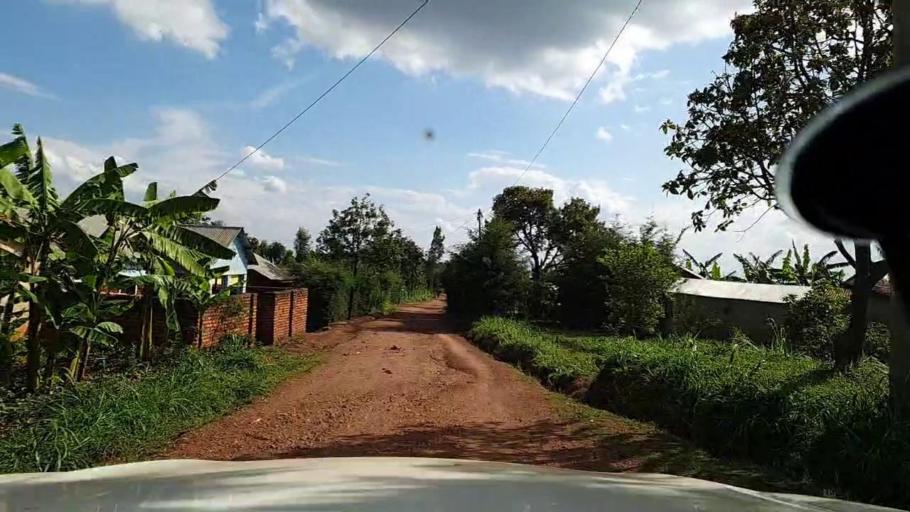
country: RW
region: Kigali
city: Kigali
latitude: -1.7953
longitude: 29.8443
